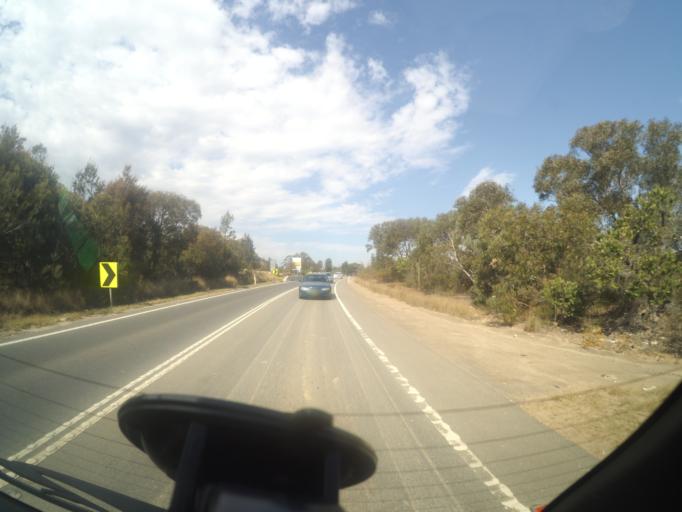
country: AU
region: New South Wales
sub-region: Liverpool
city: East Hills
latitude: -33.9921
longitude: 150.9964
